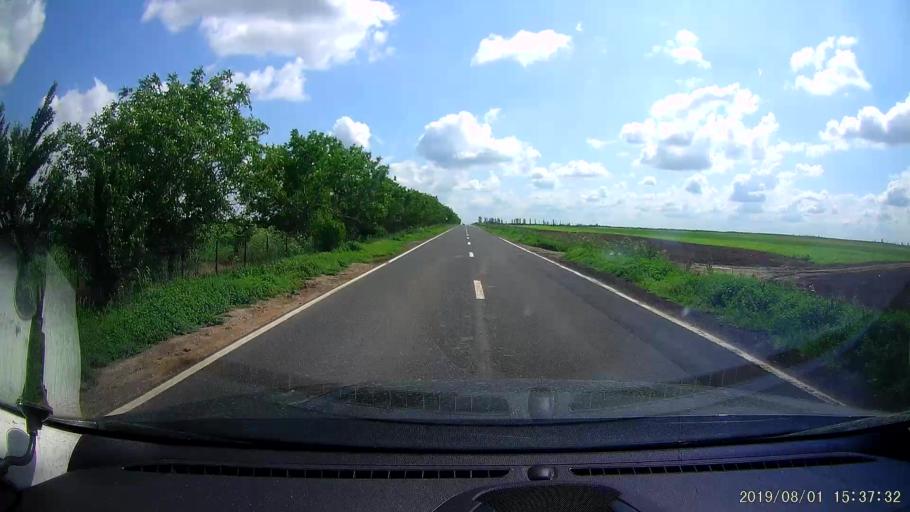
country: RO
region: Braila
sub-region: Comuna Insuratei
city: Insuratei
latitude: 44.9013
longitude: 27.5882
